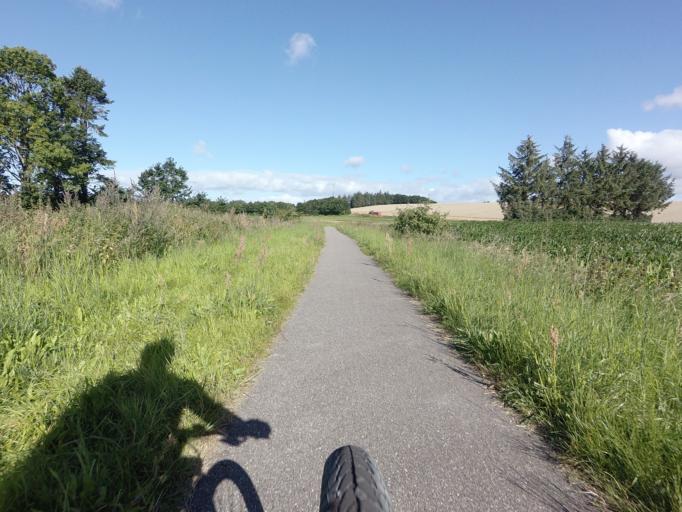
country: DK
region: Central Jutland
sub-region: Horsens Kommune
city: Horsens
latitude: 55.9584
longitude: 9.7706
